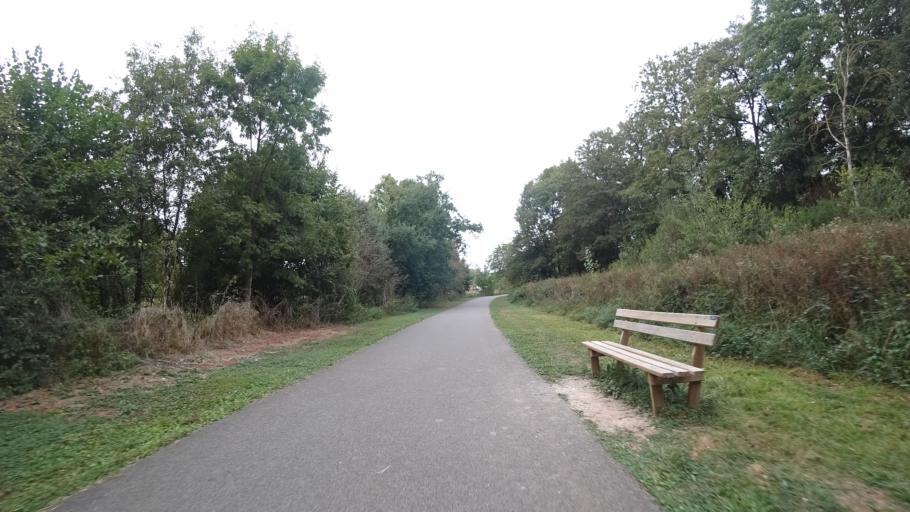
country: FR
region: Midi-Pyrenees
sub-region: Departement de l'Aveyron
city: Rodez
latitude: 44.3660
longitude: 2.5677
